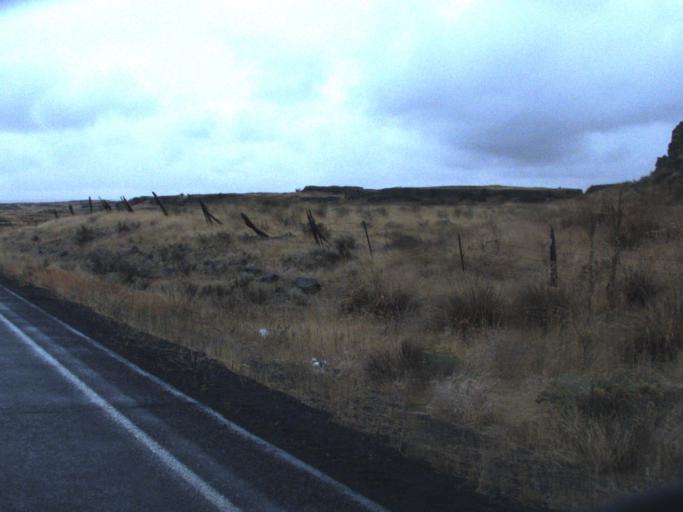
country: US
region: Washington
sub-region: Spokane County
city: Medical Lake
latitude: 47.2814
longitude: -117.9593
